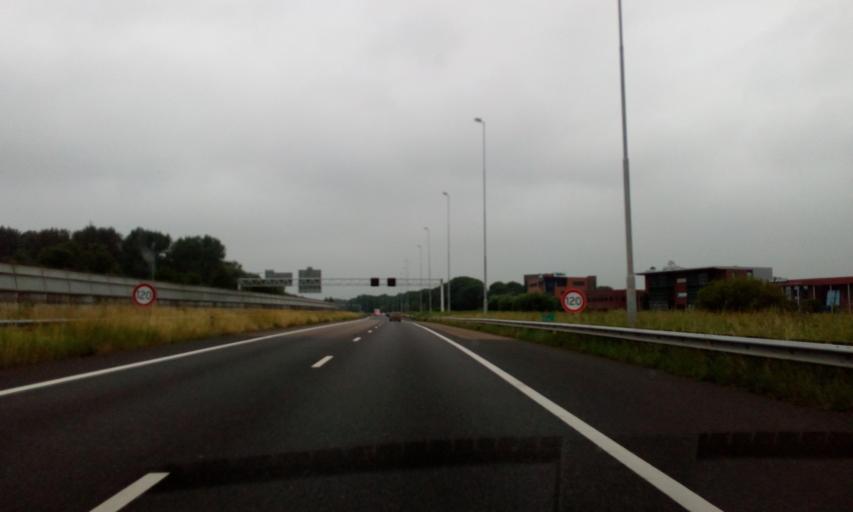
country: NL
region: South Holland
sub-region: Gemeente Sliedrecht
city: Sliedrecht
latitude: 51.8248
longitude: 4.7984
